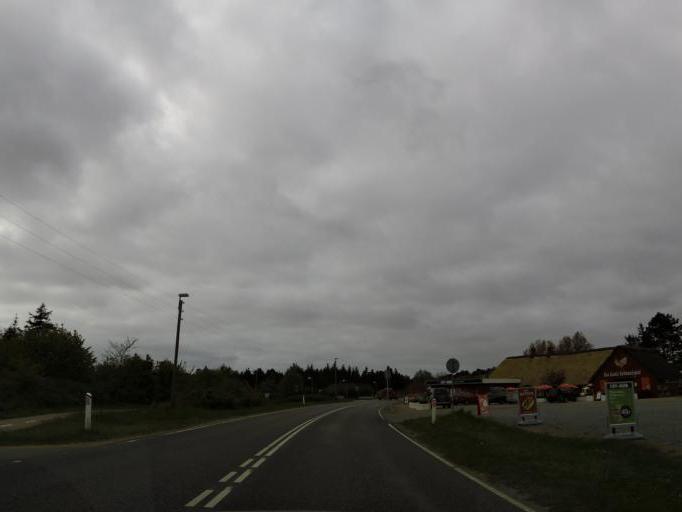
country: DE
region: Schleswig-Holstein
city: List
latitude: 55.0961
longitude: 8.5444
